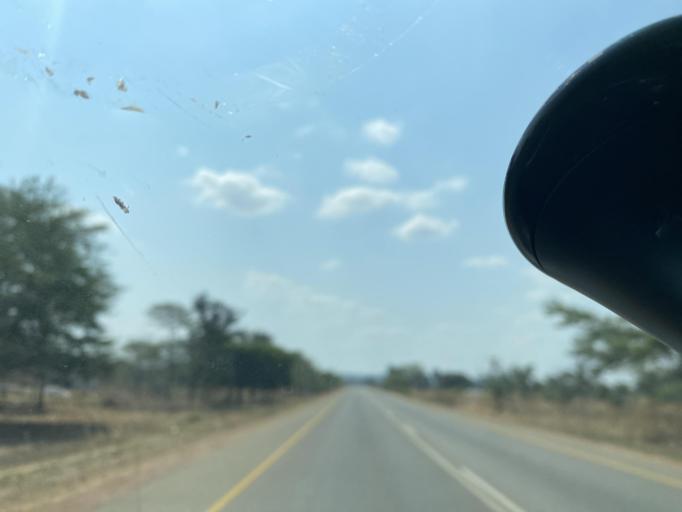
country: ZM
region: Lusaka
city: Chongwe
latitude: -15.5609
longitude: 28.6865
